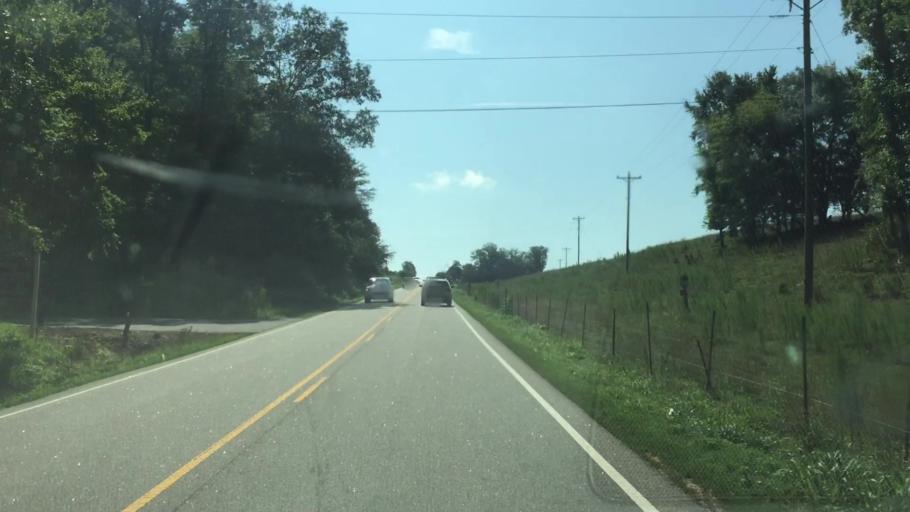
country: US
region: North Carolina
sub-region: Anson County
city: Burnsville
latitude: 35.1083
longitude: -80.3344
